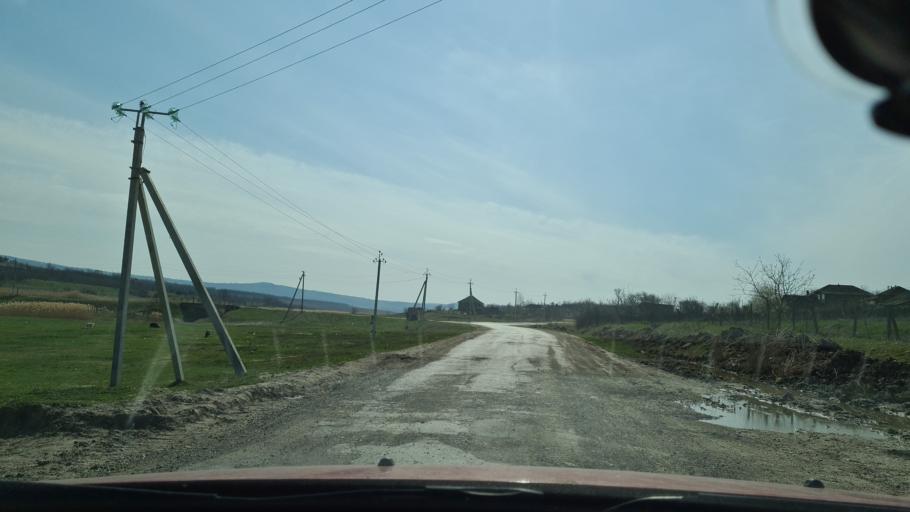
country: MD
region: Ungheni
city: Ungheni
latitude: 47.3189
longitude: 27.8990
